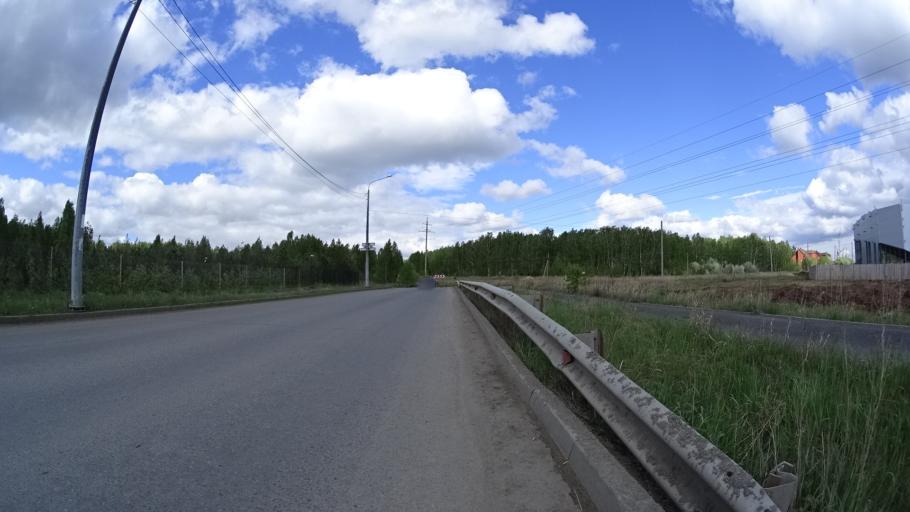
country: RU
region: Chelyabinsk
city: Sargazy
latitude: 55.1531
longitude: 61.2647
